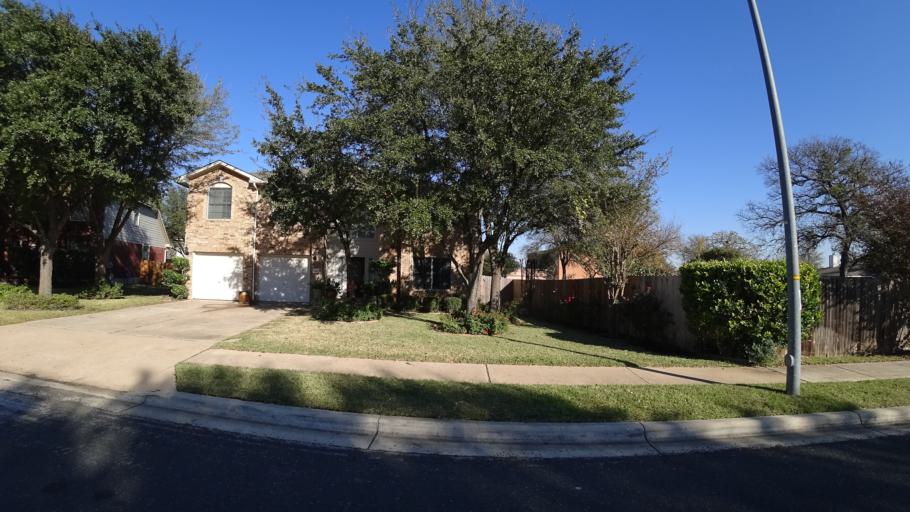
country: US
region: Texas
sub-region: Williamson County
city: Brushy Creek
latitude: 30.4886
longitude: -97.7334
